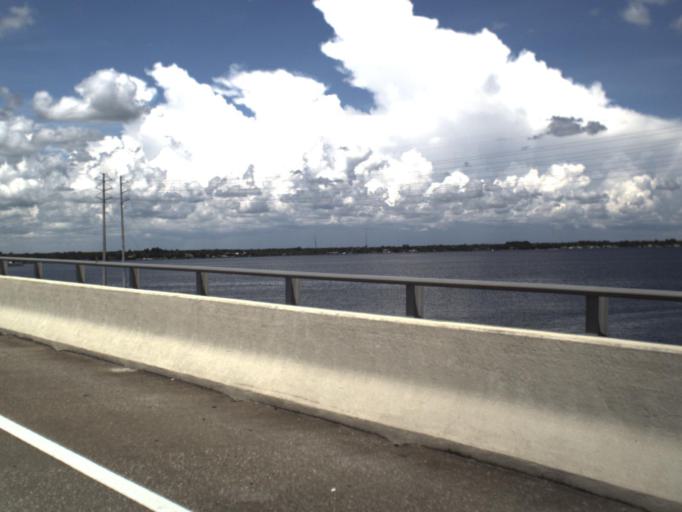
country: US
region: Florida
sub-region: Charlotte County
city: Punta Gorda
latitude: 26.9435
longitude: -82.0558
